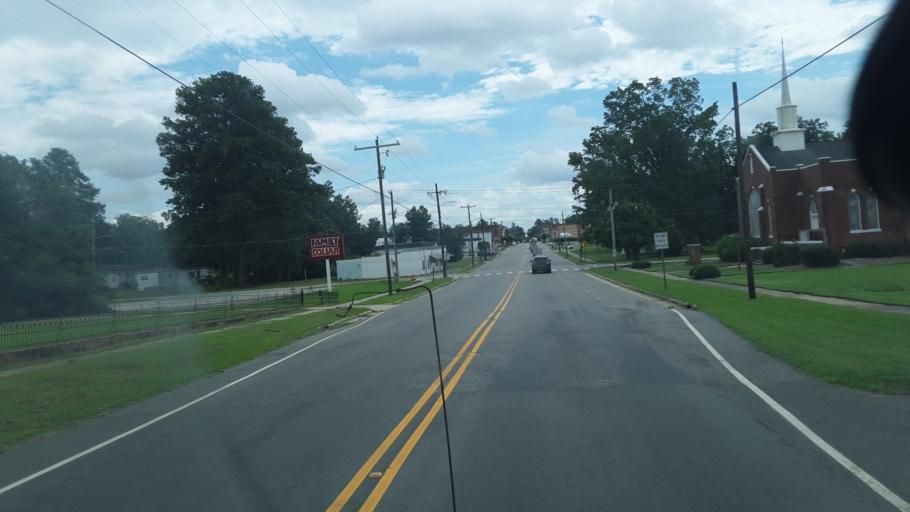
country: US
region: North Carolina
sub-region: Robeson County
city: Rowland
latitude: 34.5390
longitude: -79.2968
